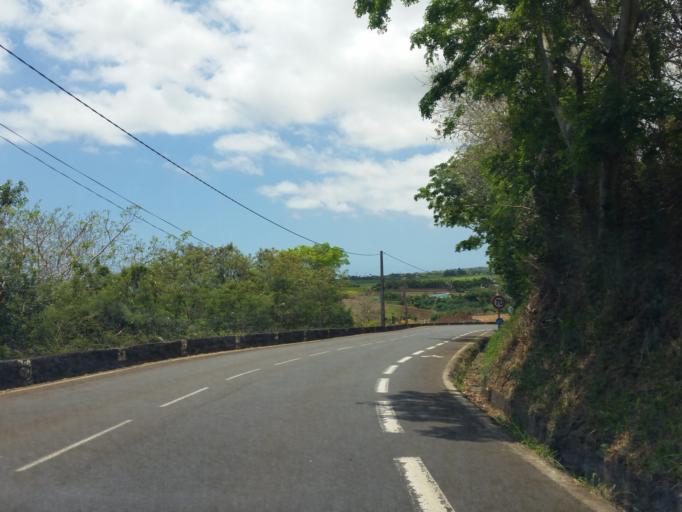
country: RE
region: Reunion
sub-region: Reunion
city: Sainte-Marie
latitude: -20.9138
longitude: 55.5286
